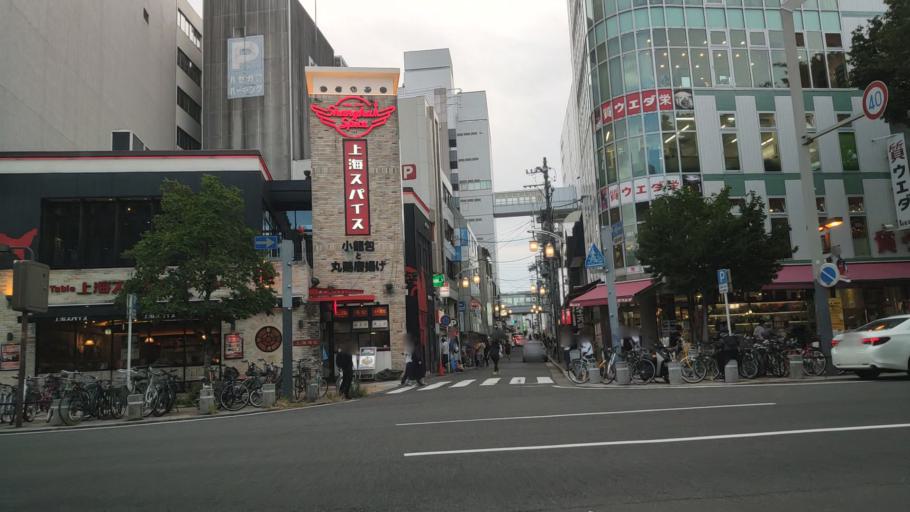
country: JP
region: Aichi
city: Nagoya-shi
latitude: 35.1629
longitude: 136.9088
